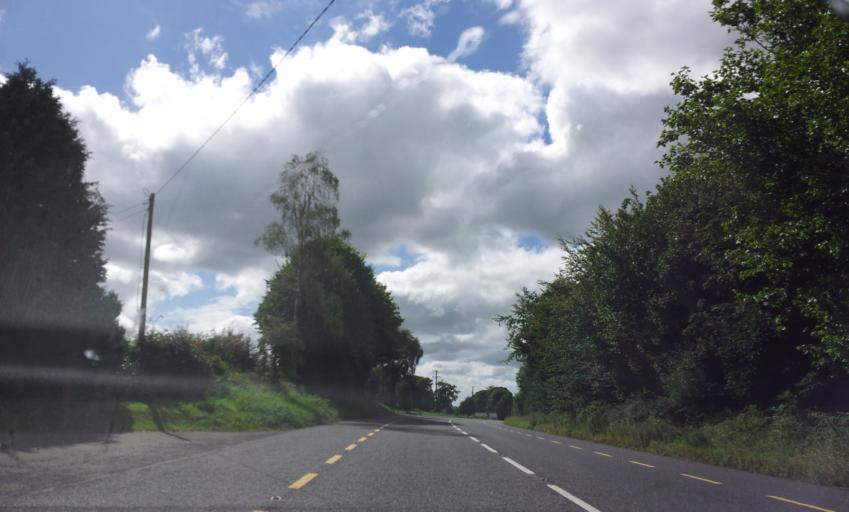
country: IE
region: Munster
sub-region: County Cork
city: Killumney
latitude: 51.8775
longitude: -8.6993
